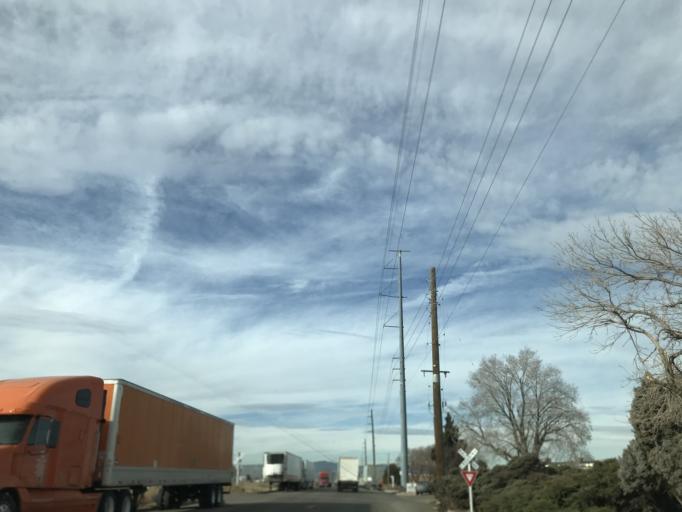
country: US
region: Colorado
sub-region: Adams County
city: Commerce City
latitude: 39.7737
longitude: -104.9102
